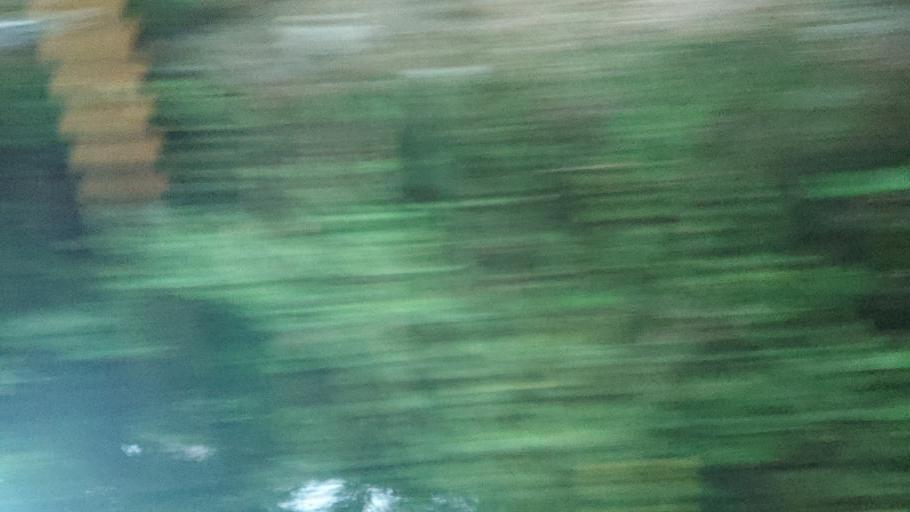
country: TW
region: Taiwan
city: Lugu
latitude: 23.5201
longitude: 120.7038
